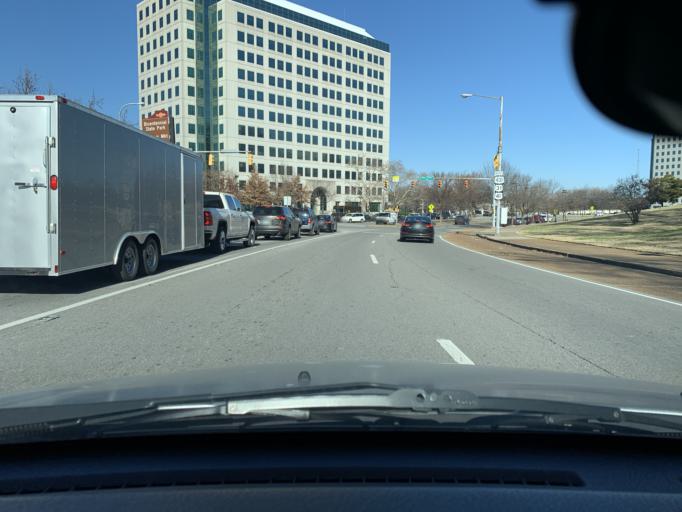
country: US
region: Tennessee
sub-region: Davidson County
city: Nashville
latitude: 36.1667
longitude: -86.7872
